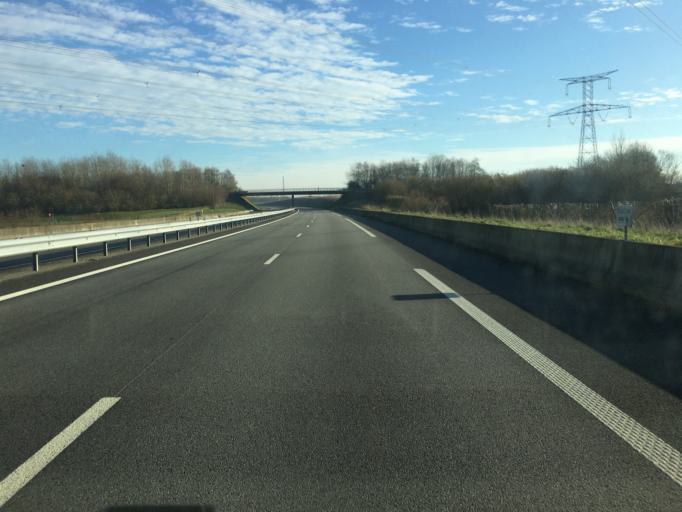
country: FR
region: Haute-Normandie
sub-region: Departement de la Seine-Maritime
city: Totes
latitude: 49.6377
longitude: 1.0336
